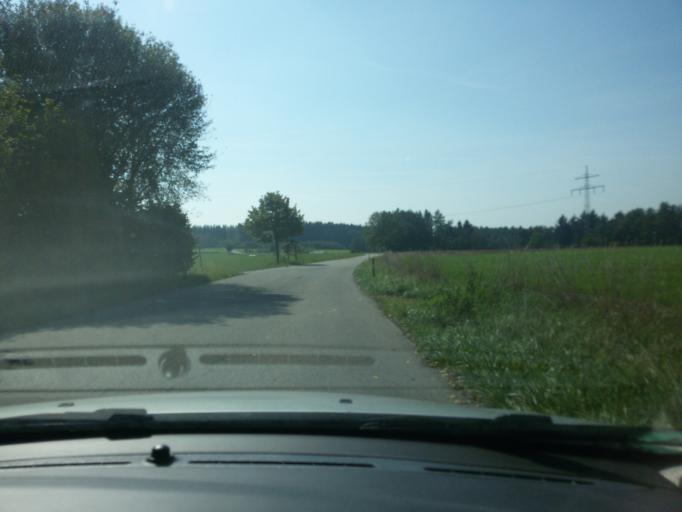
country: DE
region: Bavaria
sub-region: Swabia
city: Mittelneufnach
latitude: 48.2114
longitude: 10.6098
